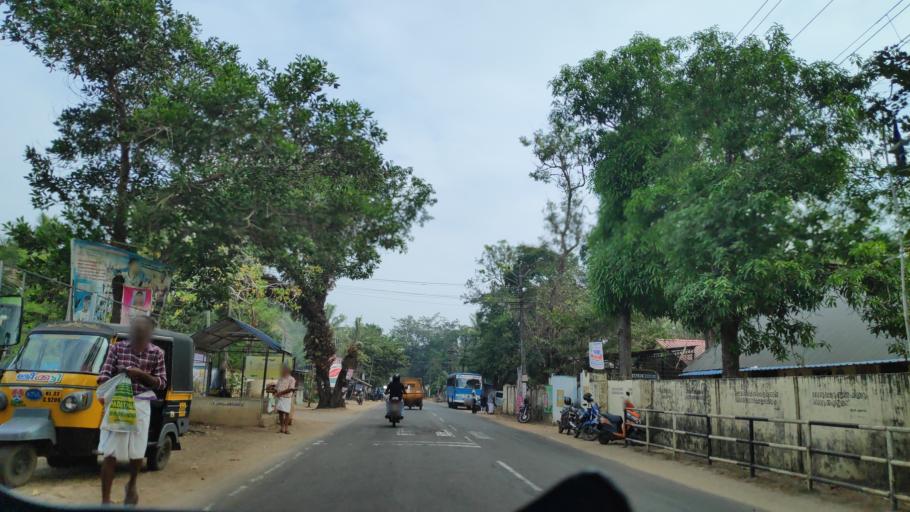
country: IN
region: Kerala
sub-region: Alappuzha
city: Vayalar
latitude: 9.7185
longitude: 76.3601
